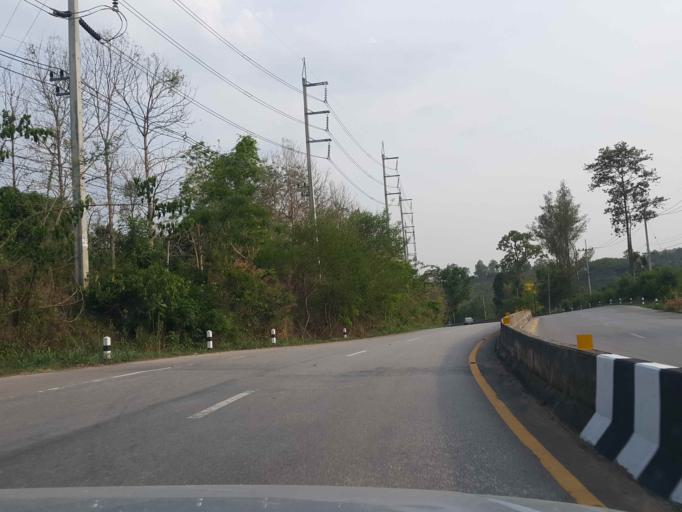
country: TH
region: Chiang Mai
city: Mae Taeng
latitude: 19.2282
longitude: 98.9698
